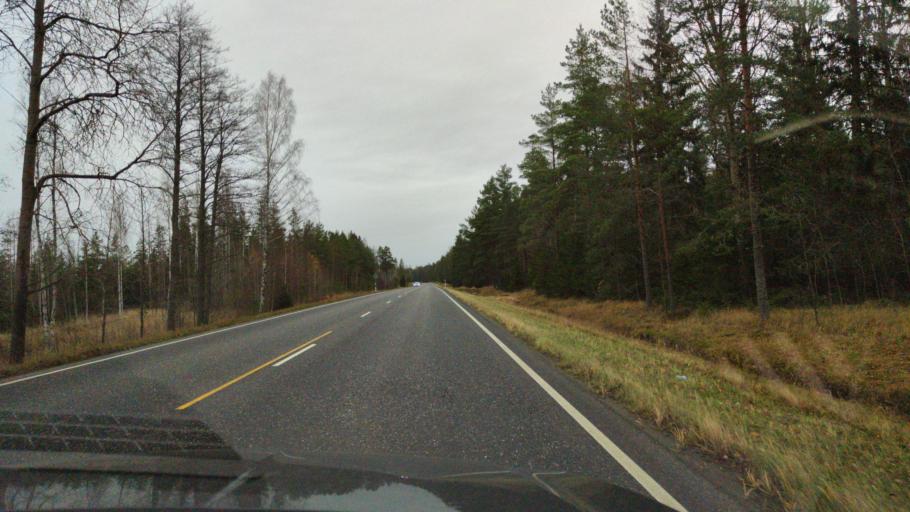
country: FI
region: Varsinais-Suomi
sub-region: Loimaa
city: Ylaene
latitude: 60.9120
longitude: 22.4135
